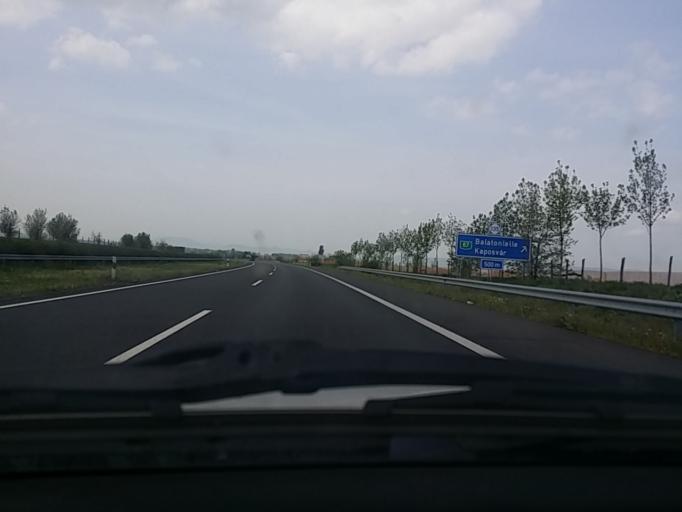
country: HU
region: Somogy
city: Balatonszarszo
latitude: 46.7930
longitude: 17.7664
